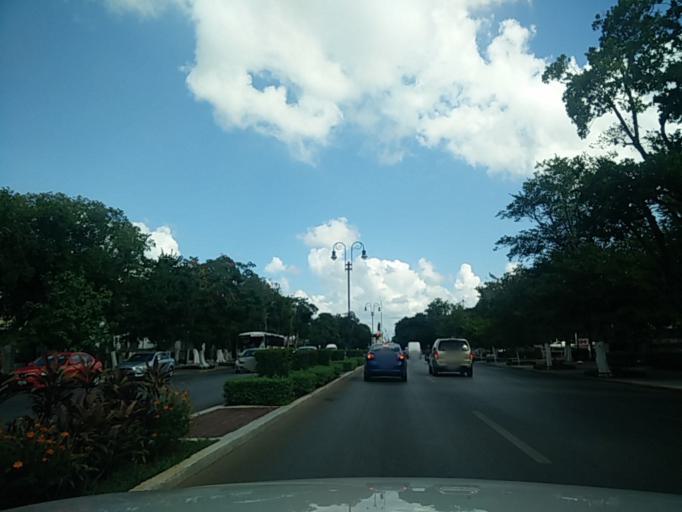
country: MX
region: Yucatan
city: Merida
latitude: 20.9846
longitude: -89.6178
